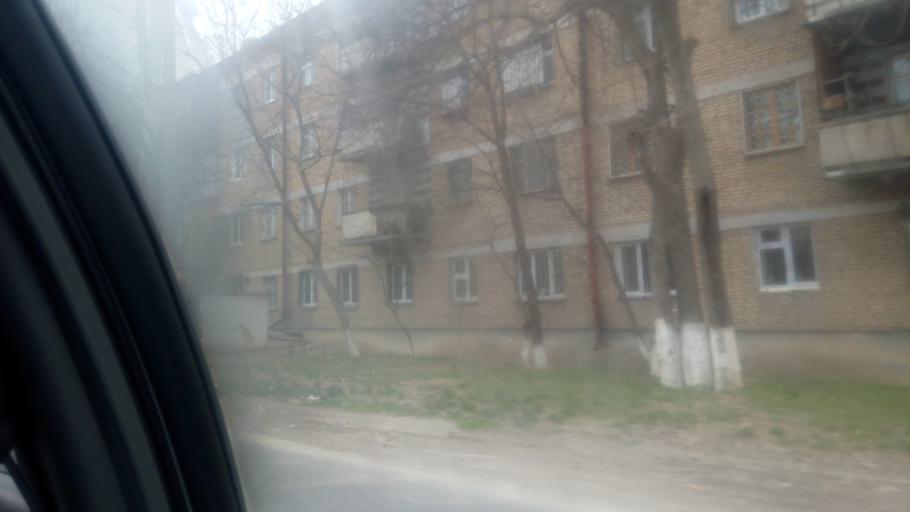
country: UZ
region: Toshkent
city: Salor
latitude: 41.3439
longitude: 69.3398
